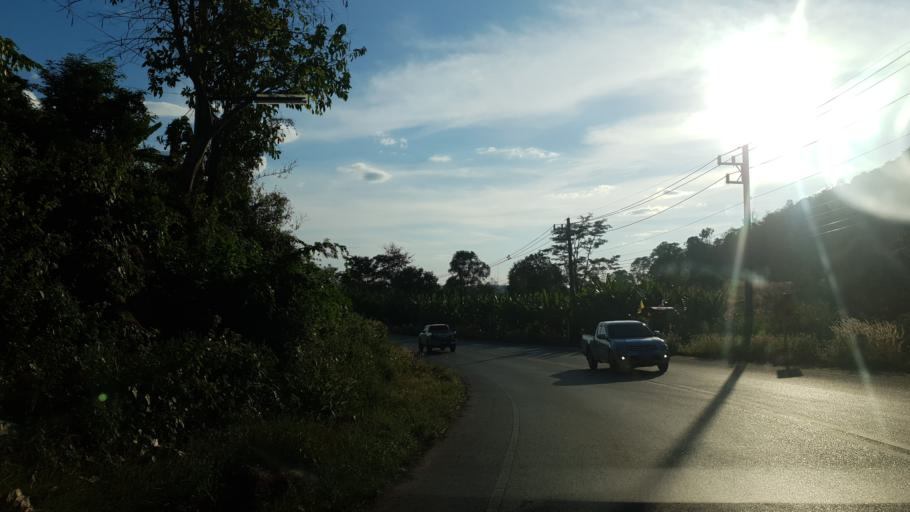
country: TH
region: Loei
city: Dan Sai
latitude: 17.2096
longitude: 101.0169
